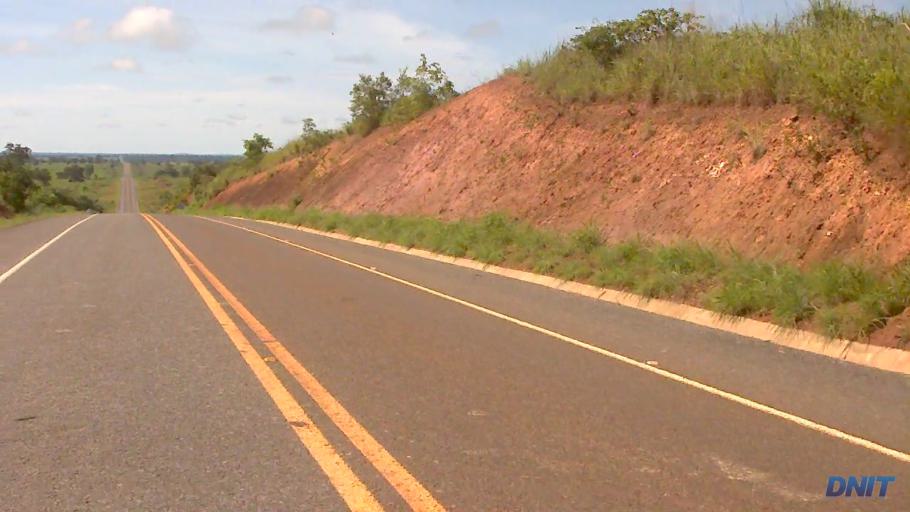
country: BR
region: Goias
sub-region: Sao Miguel Do Araguaia
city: Sao Miguel do Araguaia
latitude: -13.3271
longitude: -50.1560
